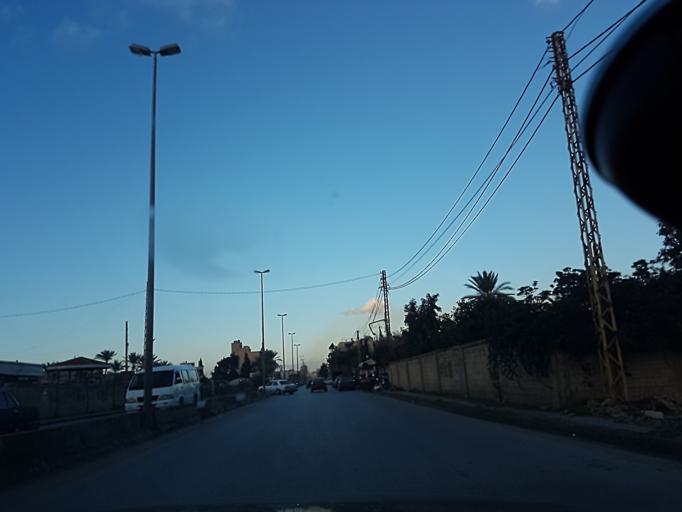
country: LB
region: Liban-Sud
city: Sidon
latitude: 33.5410
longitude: 35.3651
